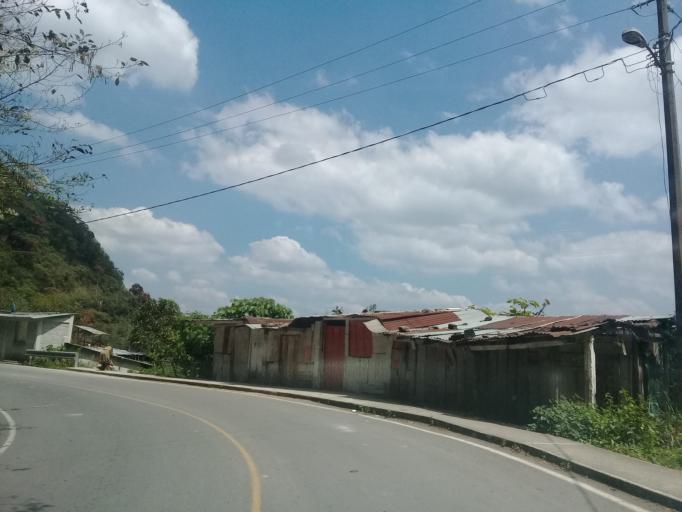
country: MX
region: Veracruz
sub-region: Tlilapan
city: Tonalixco
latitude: 18.7855
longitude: -97.0605
